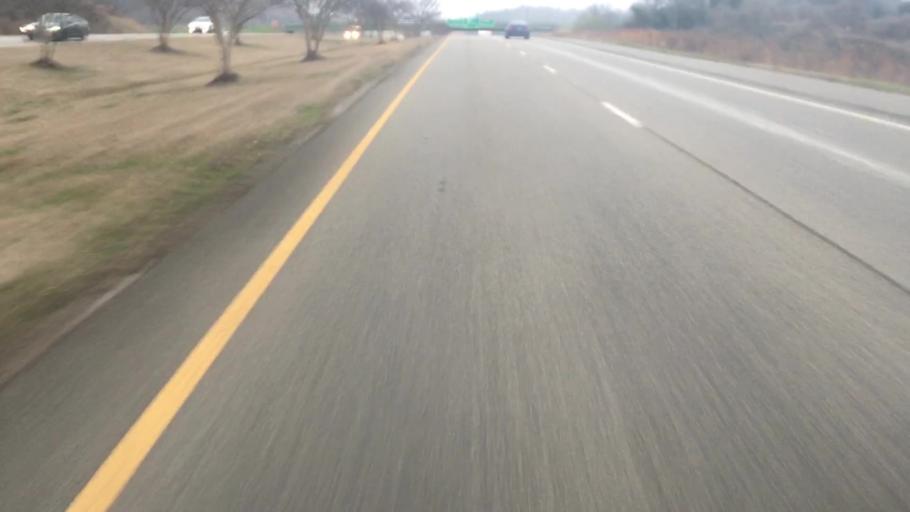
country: US
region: Alabama
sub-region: Jefferson County
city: Fultondale
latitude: 33.5817
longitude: -86.8049
